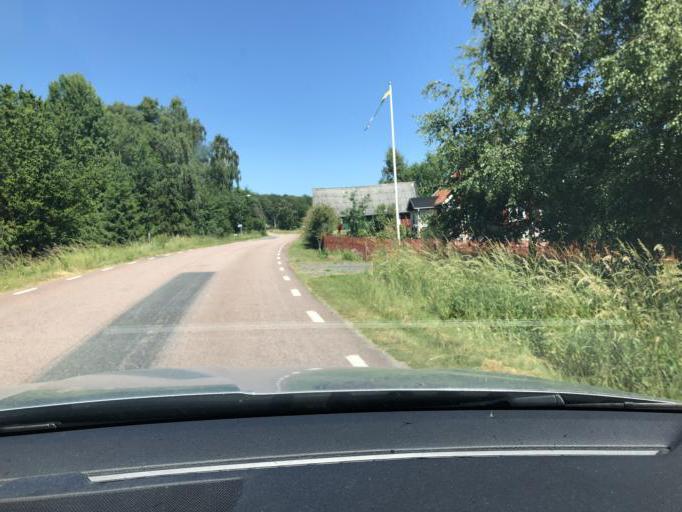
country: SE
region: Blekinge
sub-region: Olofstroms Kommun
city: Jamshog
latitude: 56.1645
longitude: 14.5986
